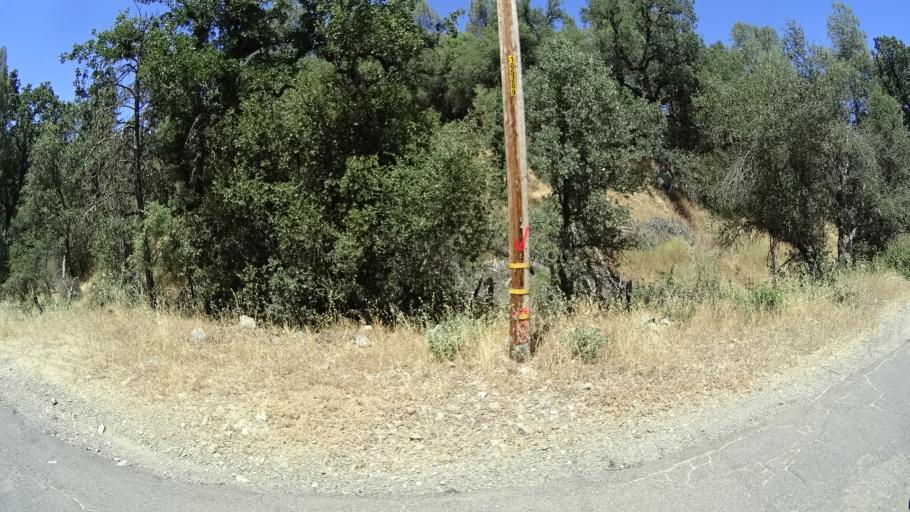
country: US
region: California
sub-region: Calaveras County
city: Mountain Ranch
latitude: 38.2634
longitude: -120.4808
